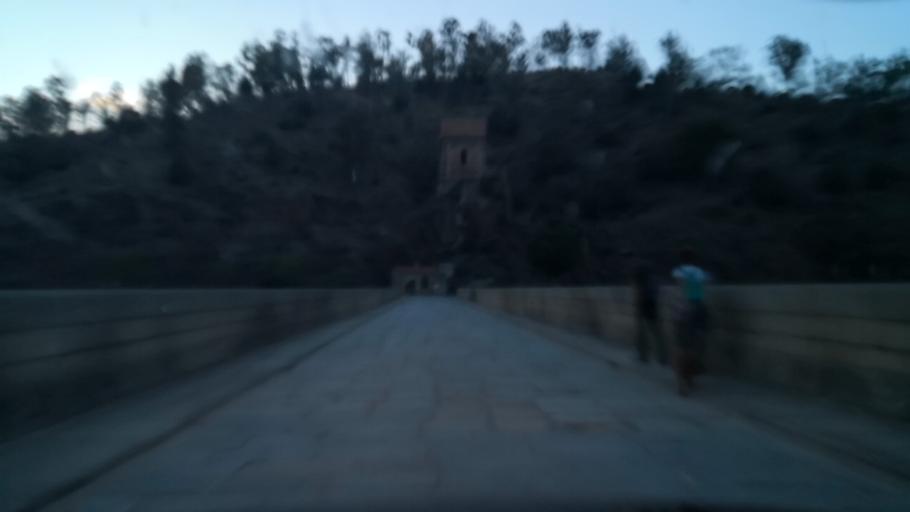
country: ES
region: Extremadura
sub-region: Provincia de Caceres
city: Alcantara
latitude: 39.7225
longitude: -6.8925
